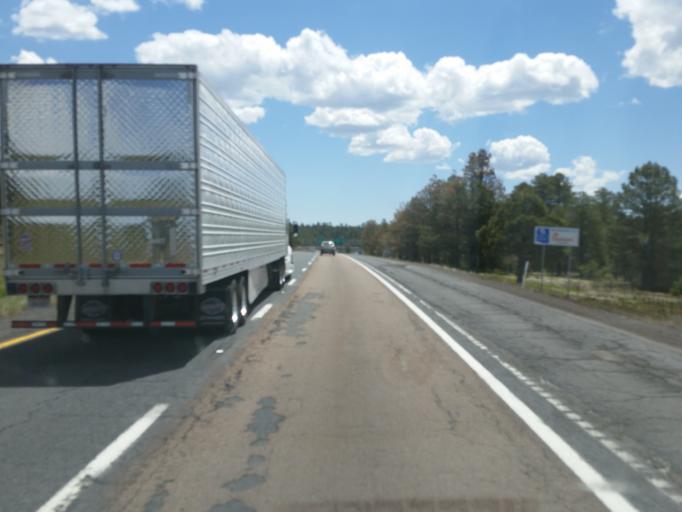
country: US
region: Arizona
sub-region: Coconino County
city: Flagstaff
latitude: 35.1988
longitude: -111.7515
